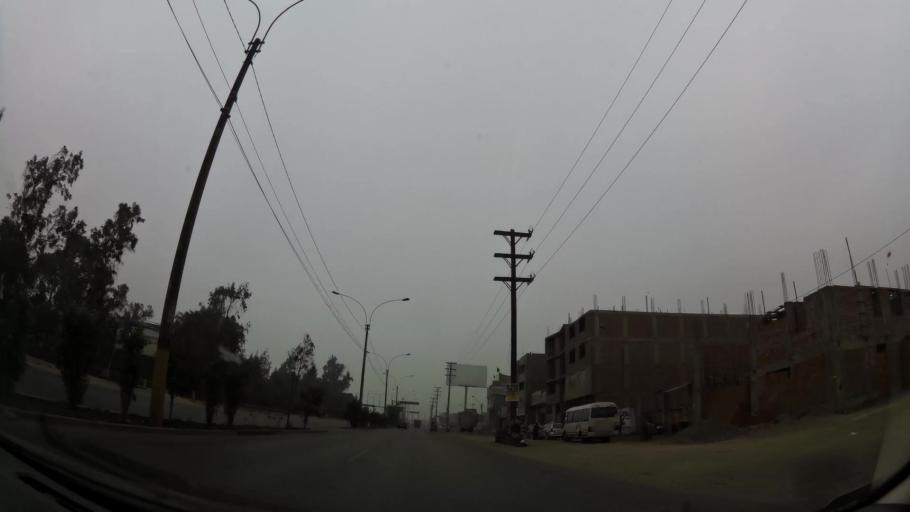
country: PE
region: Lima
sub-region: Lima
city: Santa Maria
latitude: -11.9976
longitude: -76.8360
